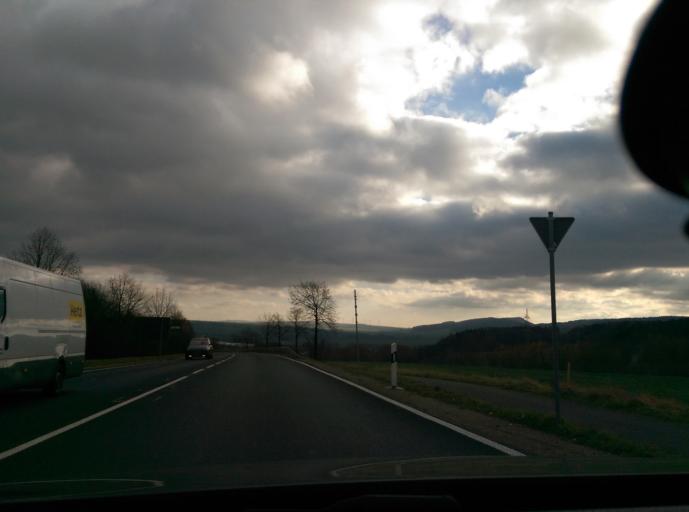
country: DE
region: Thuringia
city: Eisenach
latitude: 50.9953
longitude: 10.3563
